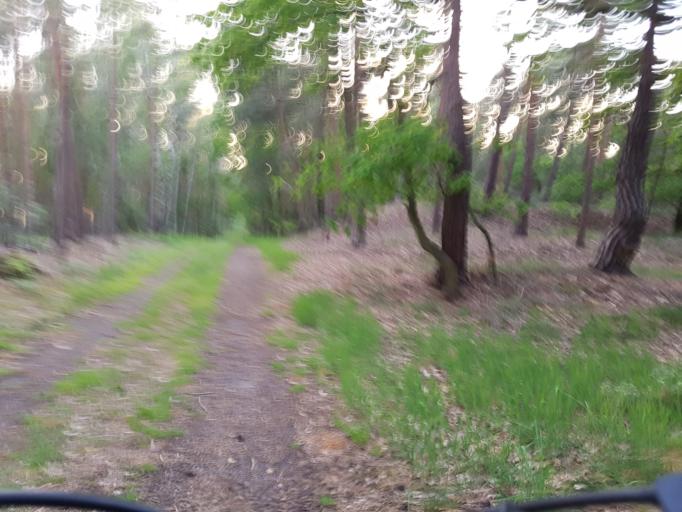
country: DE
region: Brandenburg
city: Bad Liebenwerda
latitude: 51.5562
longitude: 13.4071
